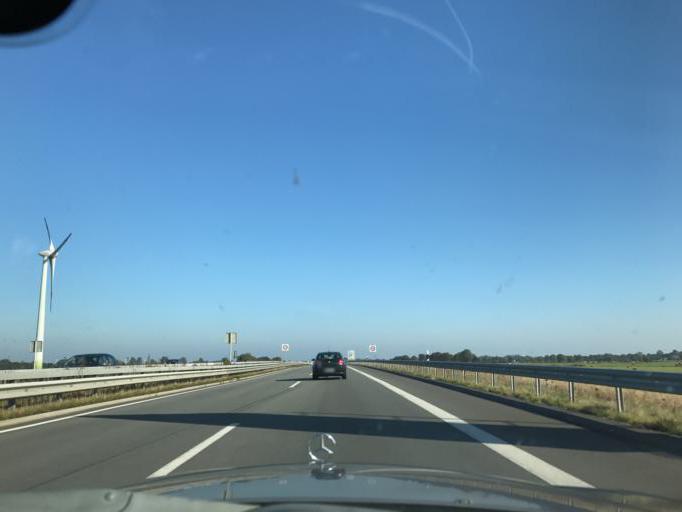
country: DE
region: Lower Saxony
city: Jemgum
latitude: 53.2231
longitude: 7.3770
